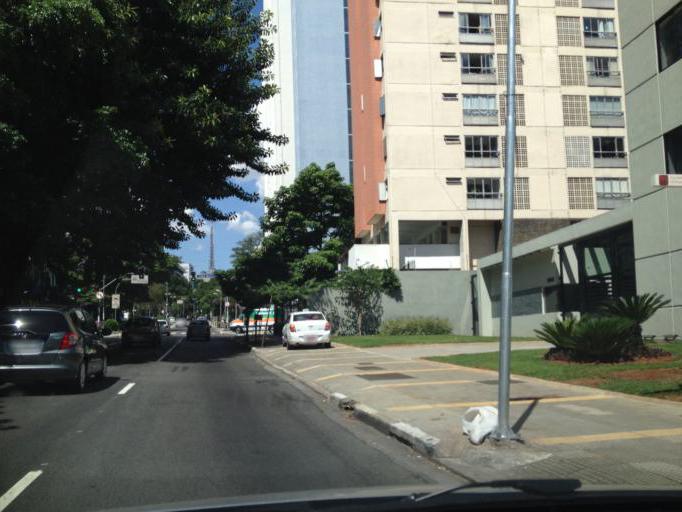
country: BR
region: Sao Paulo
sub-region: Sao Paulo
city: Sao Paulo
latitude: -23.5635
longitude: -46.6762
